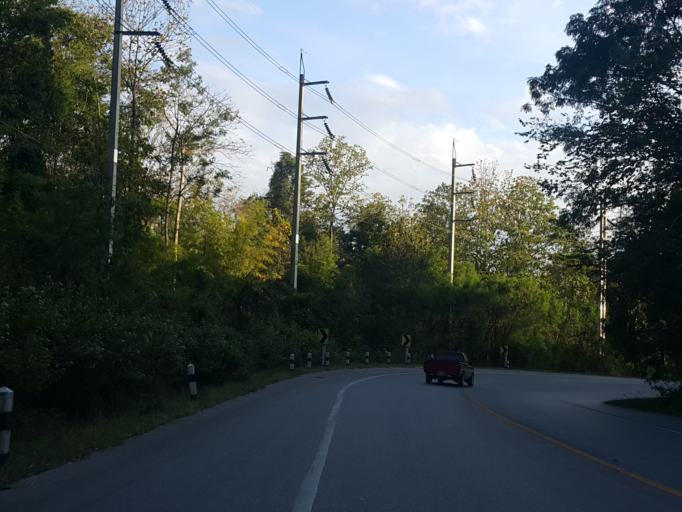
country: TH
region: Lampang
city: Lampang
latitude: 18.4864
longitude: 99.5479
